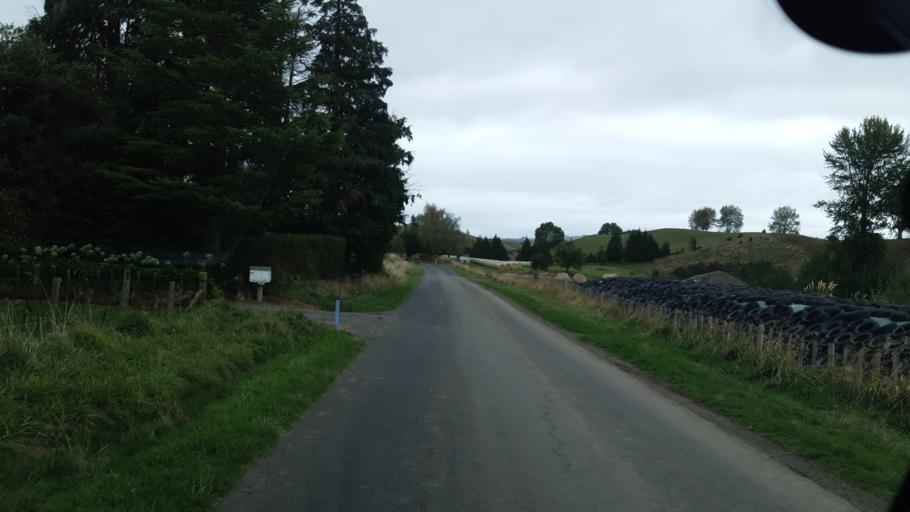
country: NZ
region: Manawatu-Wanganui
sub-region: Ruapehu District
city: Waiouru
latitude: -39.5557
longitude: 175.6219
